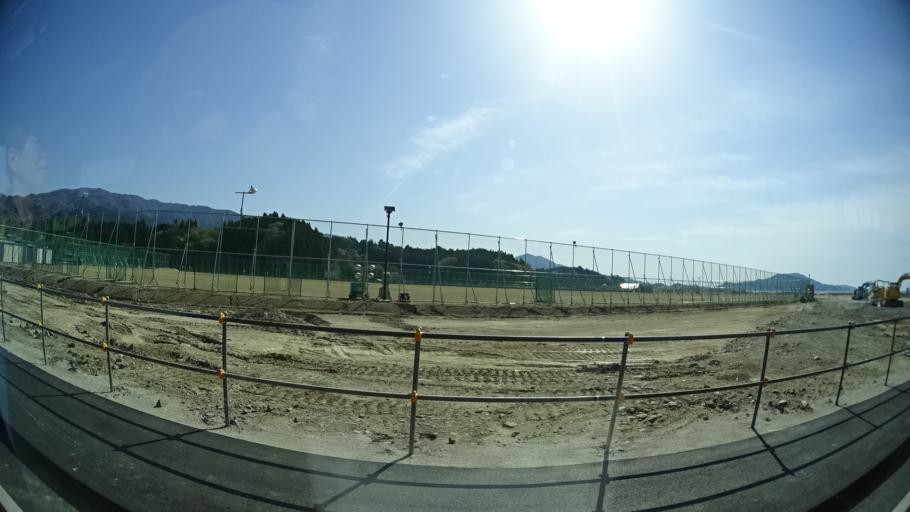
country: JP
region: Iwate
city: Ofunato
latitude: 39.0185
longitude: 141.6219
